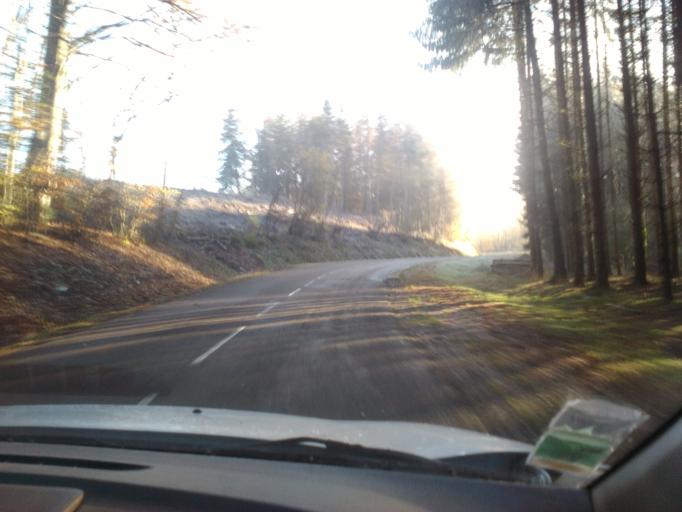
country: FR
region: Lorraine
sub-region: Departement des Vosges
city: Uzemain
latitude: 48.0570
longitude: 6.3565
